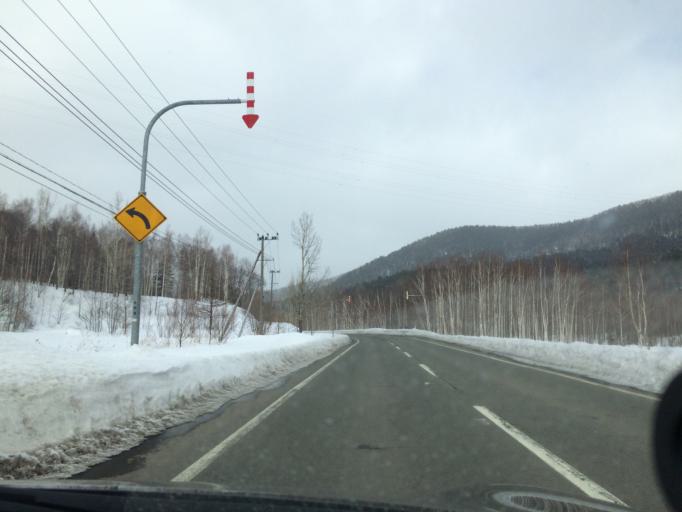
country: JP
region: Hokkaido
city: Shimo-furano
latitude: 43.0496
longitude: 142.5330
